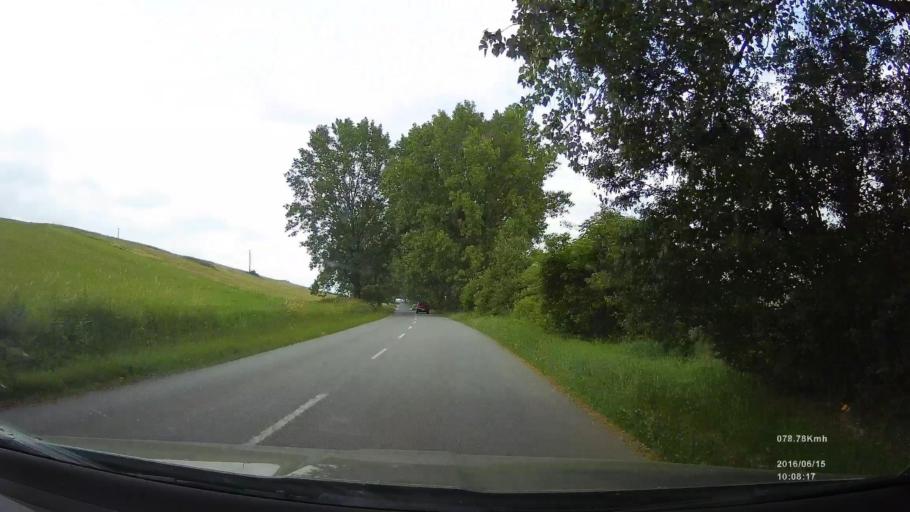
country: SK
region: Kosicky
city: Kosice
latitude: 48.7690
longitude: 21.3307
